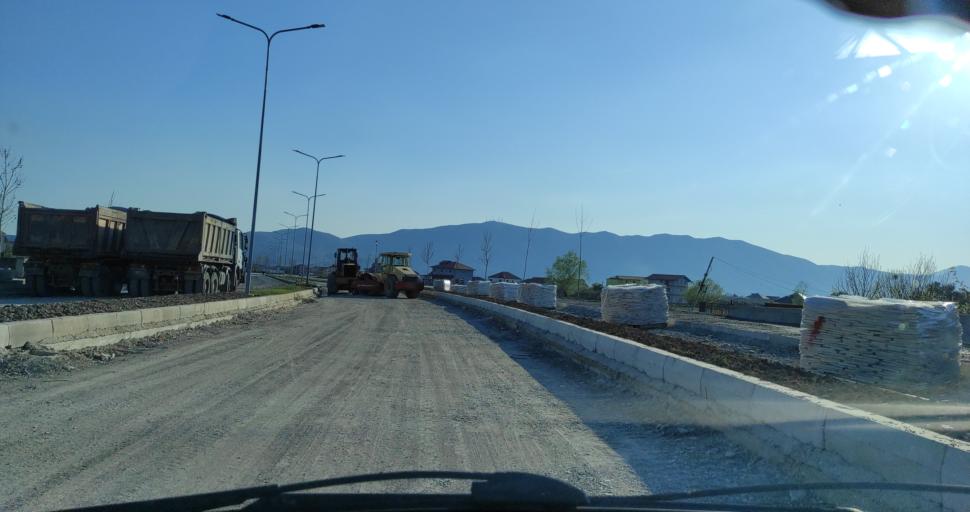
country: AL
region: Shkoder
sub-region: Rrethi i Shkodres
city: Shkoder
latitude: 42.0884
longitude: 19.5055
